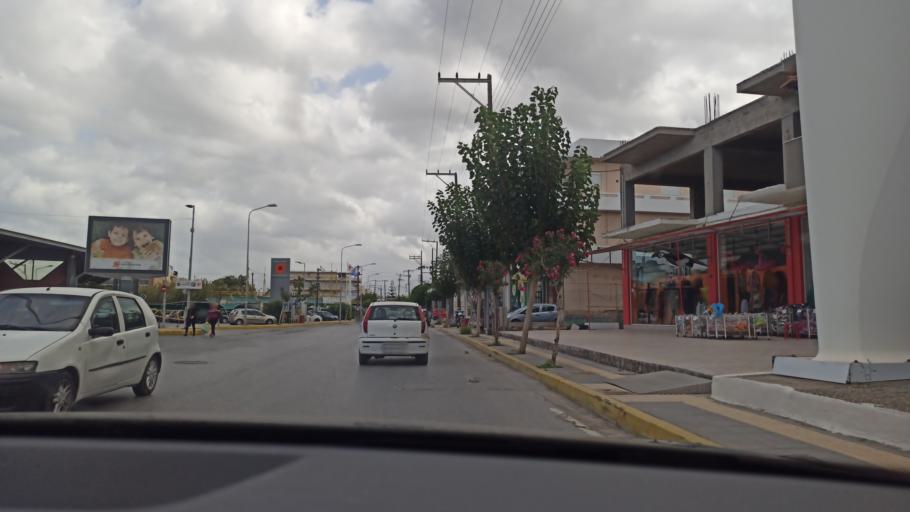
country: GR
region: Crete
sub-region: Nomos Irakleiou
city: Gazi
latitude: 35.3342
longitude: 25.0945
